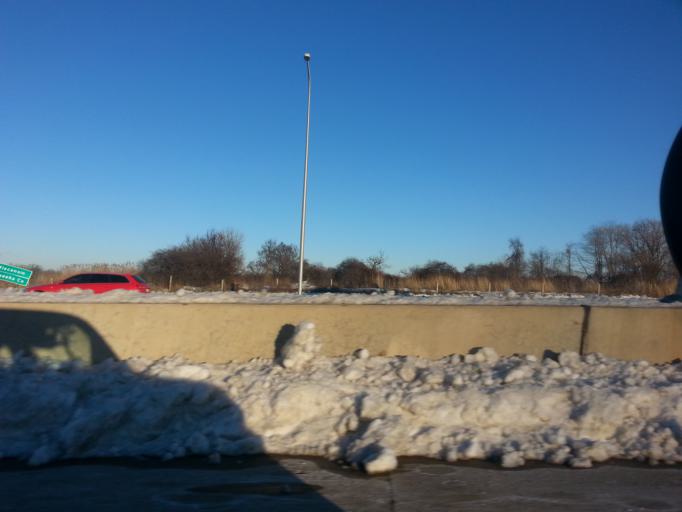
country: US
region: Wisconsin
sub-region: Kenosha County
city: Pleasant Prairie
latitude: 42.4944
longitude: -87.9499
